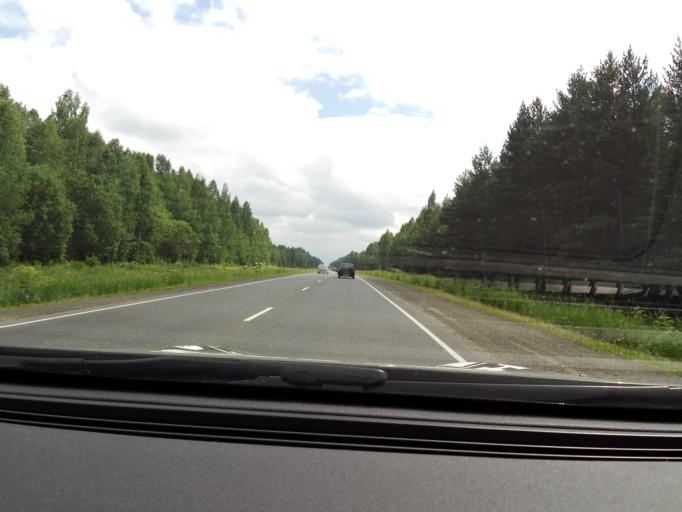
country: RU
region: Perm
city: Kungur
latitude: 57.4238
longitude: 56.8404
